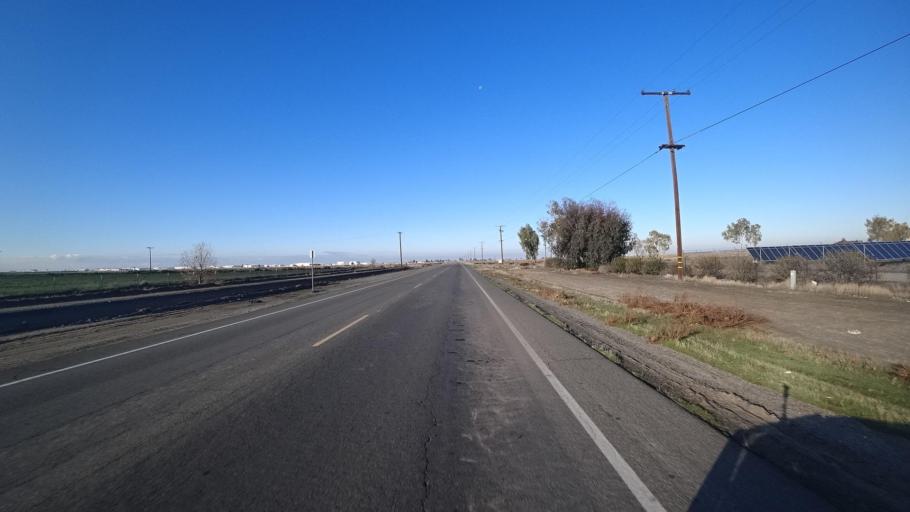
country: US
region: California
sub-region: Kern County
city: Delano
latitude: 35.7759
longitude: -119.3105
